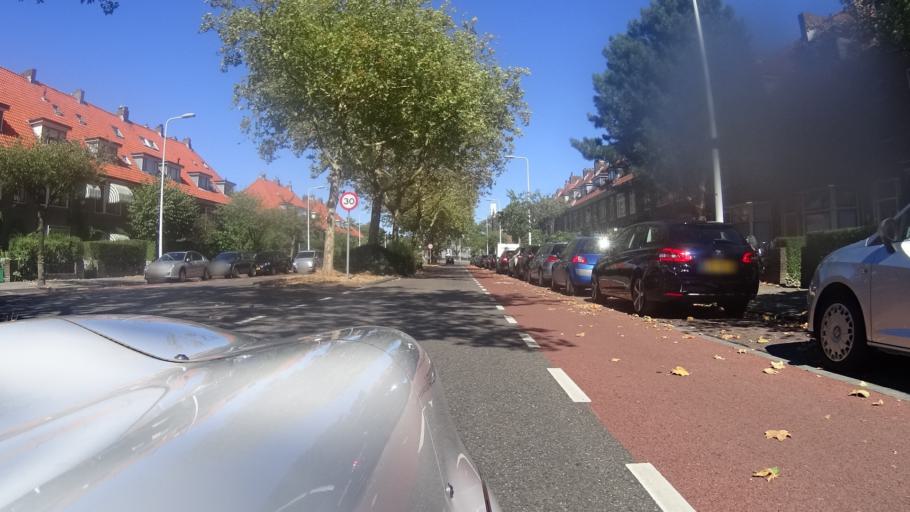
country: NL
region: South Holland
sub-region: Gemeente Leiden
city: Leiden
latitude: 52.1476
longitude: 4.4982
